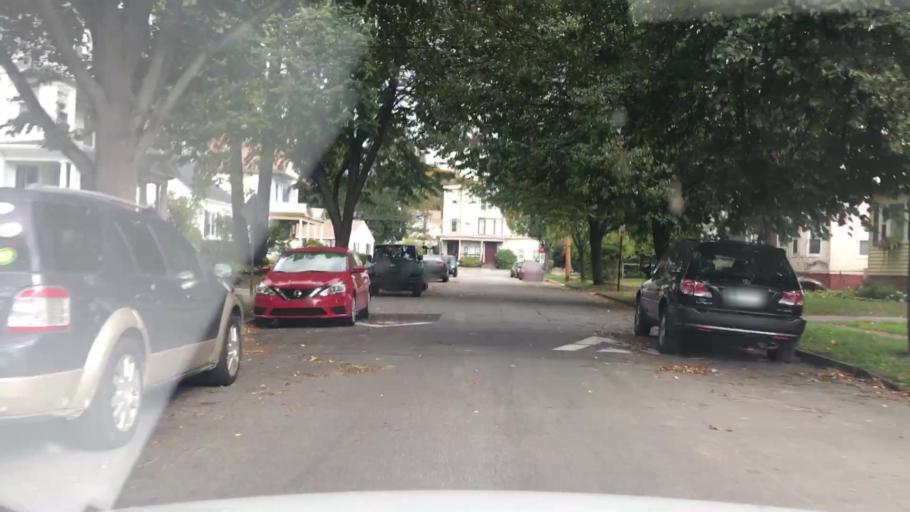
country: US
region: Maine
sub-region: Cumberland County
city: Portland
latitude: 43.6634
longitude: -70.2878
